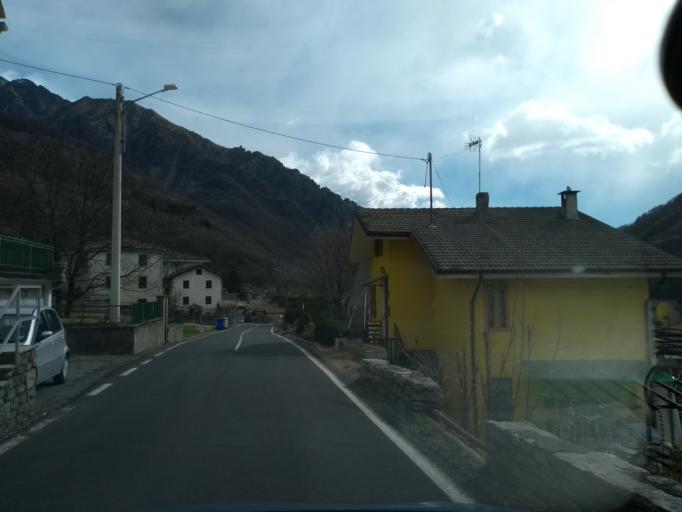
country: IT
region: Piedmont
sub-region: Provincia di Torino
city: Chialamberto
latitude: 45.3649
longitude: 7.3360
